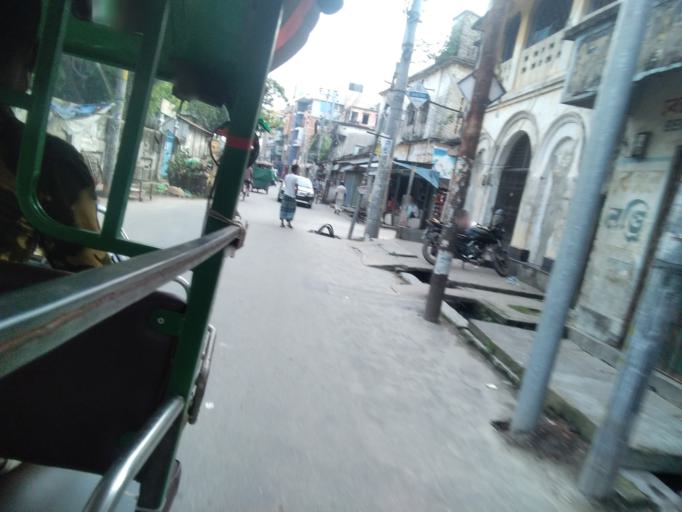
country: BD
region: Khulna
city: Khulna
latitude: 22.8146
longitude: 89.5619
